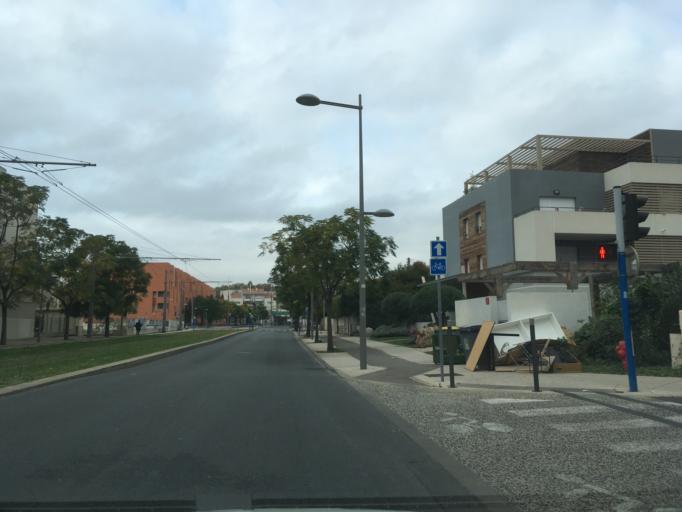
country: FR
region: Languedoc-Roussillon
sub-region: Departement de l'Herault
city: Montpellier
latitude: 43.5915
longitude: 3.8823
